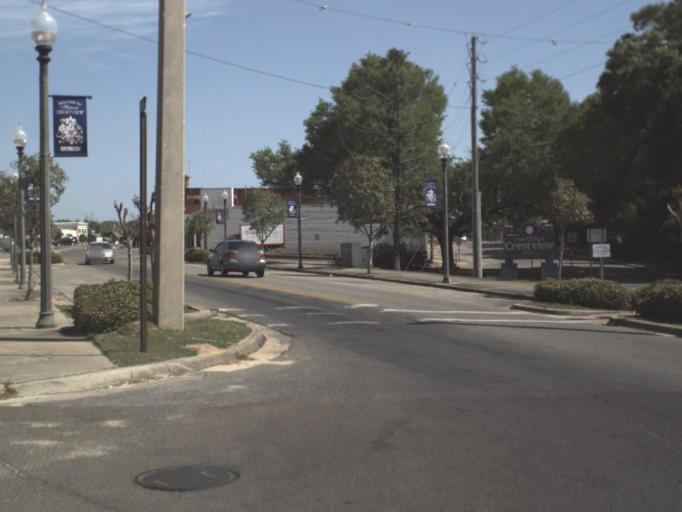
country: US
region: Florida
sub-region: Okaloosa County
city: Crestview
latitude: 30.7618
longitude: -86.5742
